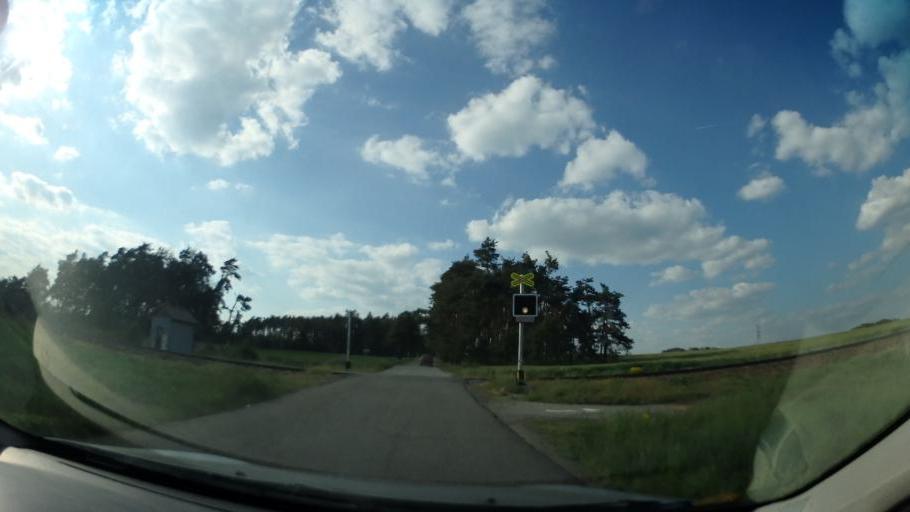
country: CZ
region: Vysocina
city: Vladislav
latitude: 49.2140
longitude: 16.0241
